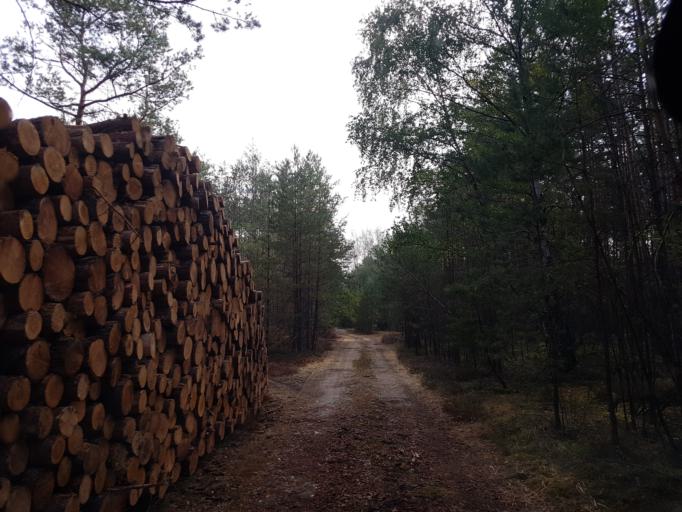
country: DE
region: Brandenburg
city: Finsterwalde
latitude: 51.5992
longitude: 13.7581
